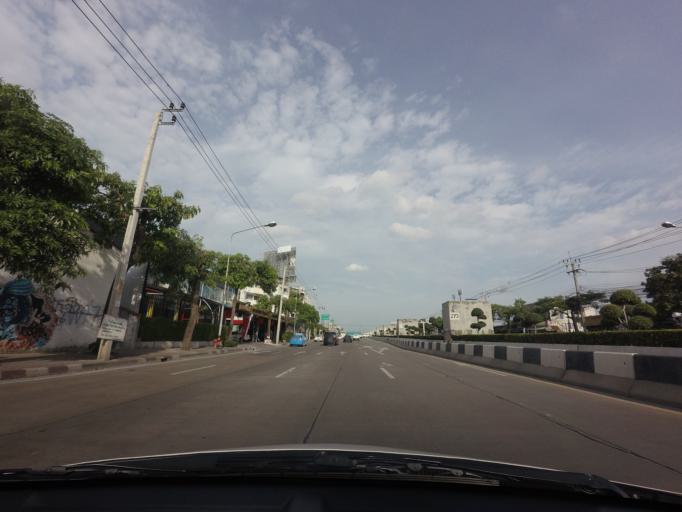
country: TH
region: Bangkok
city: Khan Na Yao
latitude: 13.8128
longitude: 100.6466
